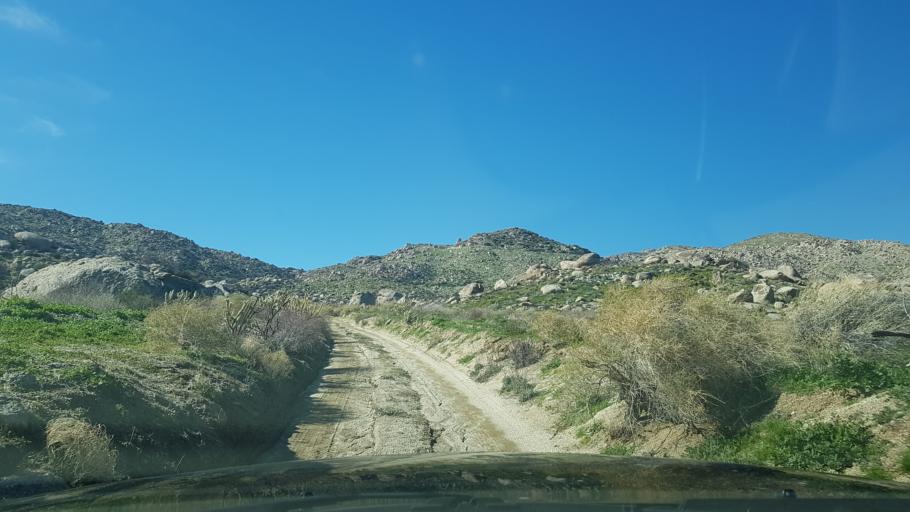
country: US
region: California
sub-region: San Diego County
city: Borrego Springs
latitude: 33.2107
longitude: -116.4576
